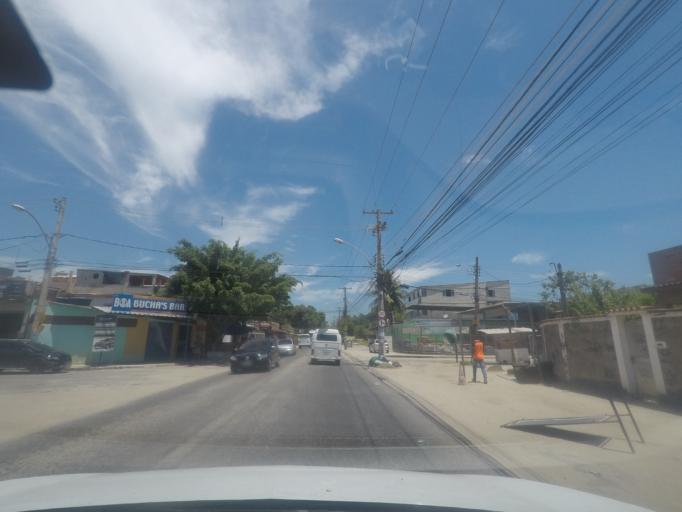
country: BR
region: Rio de Janeiro
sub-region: Itaguai
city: Itaguai
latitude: -22.9418
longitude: -43.6842
